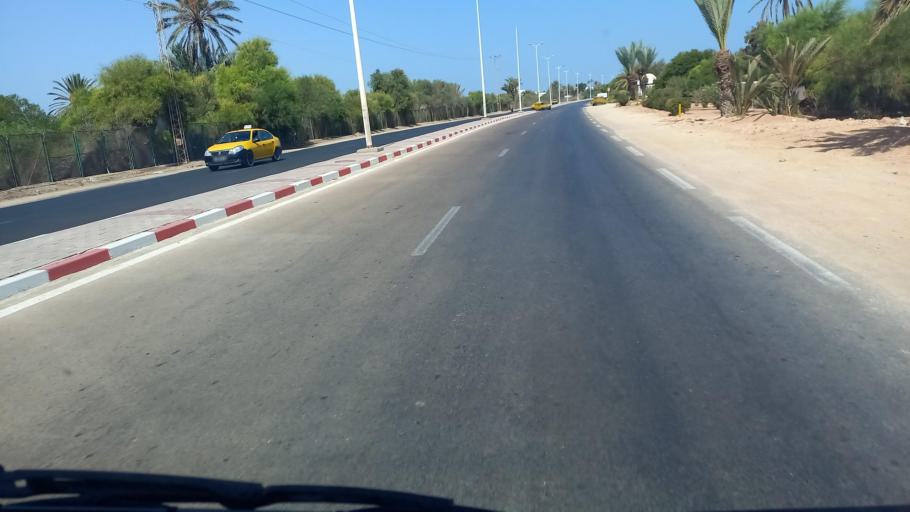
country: TN
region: Madanin
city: Midoun
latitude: 33.8295
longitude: 11.0084
